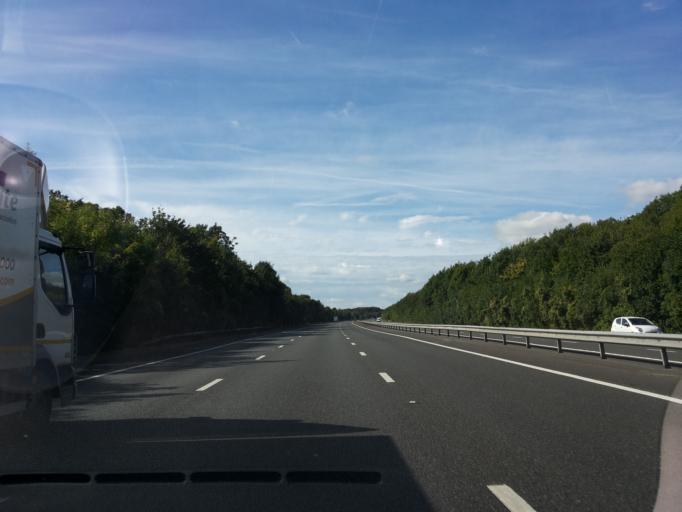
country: GB
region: England
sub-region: Kent
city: Borough Green
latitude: 51.3072
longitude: 0.3363
